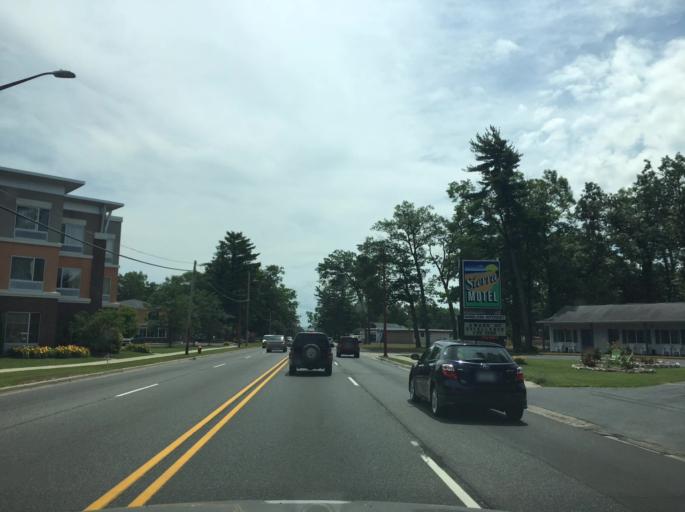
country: US
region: Michigan
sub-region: Grand Traverse County
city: Traverse City
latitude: 44.7628
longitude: -85.5861
